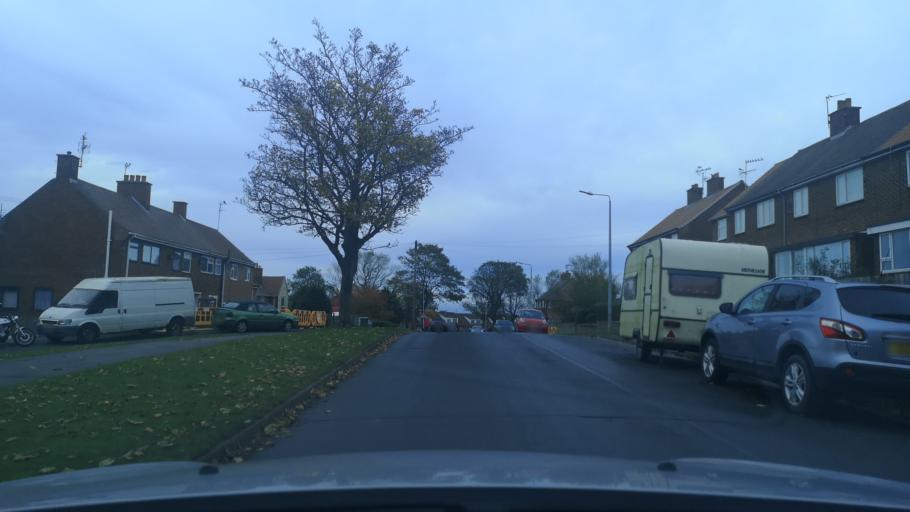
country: GB
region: England
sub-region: East Riding of Yorkshire
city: Hornsea
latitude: 53.9048
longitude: -0.1678
